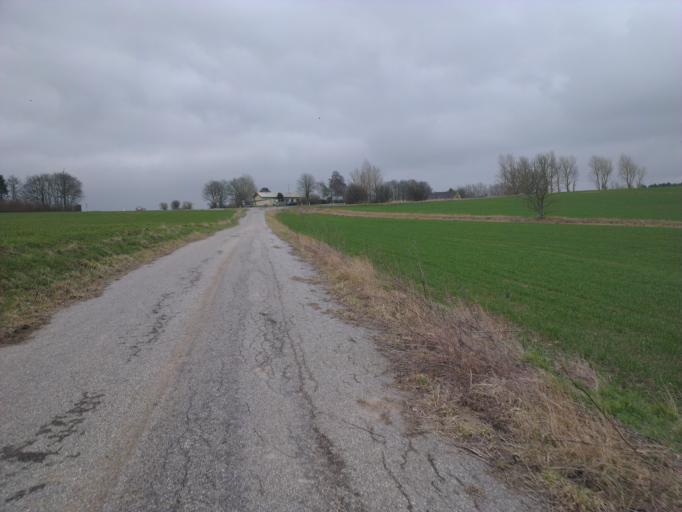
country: DK
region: Capital Region
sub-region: Frederikssund Kommune
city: Frederikssund
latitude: 55.8746
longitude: 12.0810
